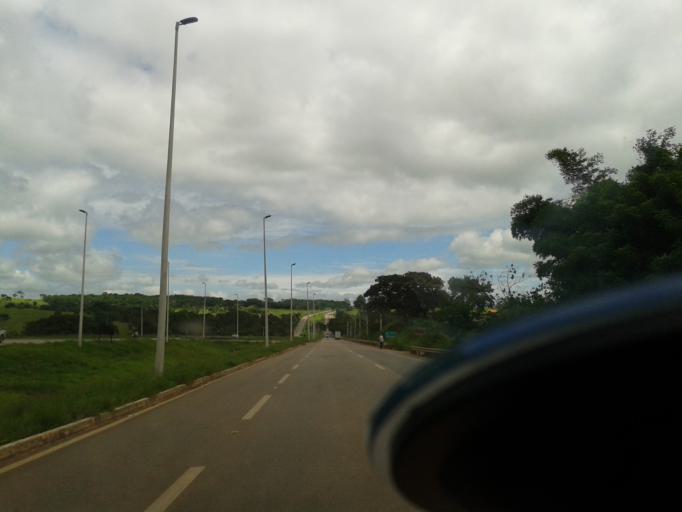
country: BR
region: Goias
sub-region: Inhumas
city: Inhumas
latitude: -16.3553
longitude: -49.5119
